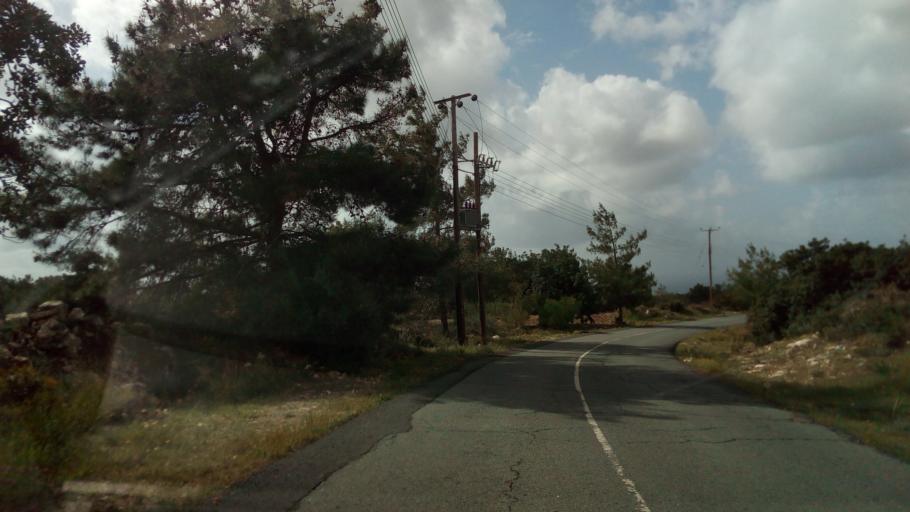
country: CY
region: Limassol
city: Sotira
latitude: 34.7165
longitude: 32.8664
